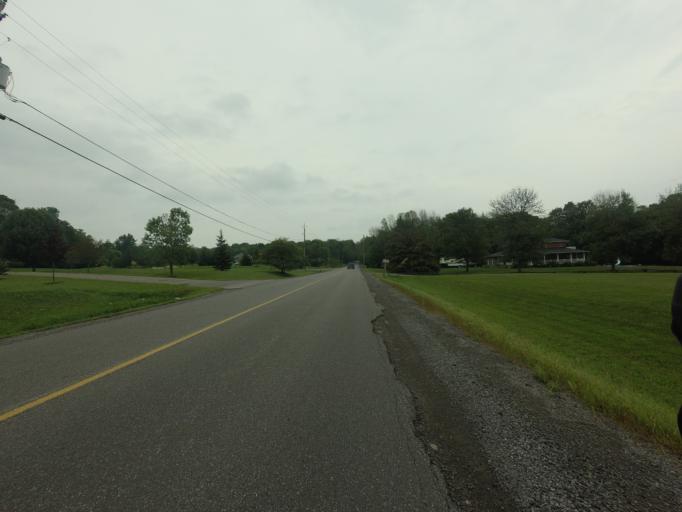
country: CA
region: Ontario
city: Bells Corners
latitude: 45.3393
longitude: -75.9951
